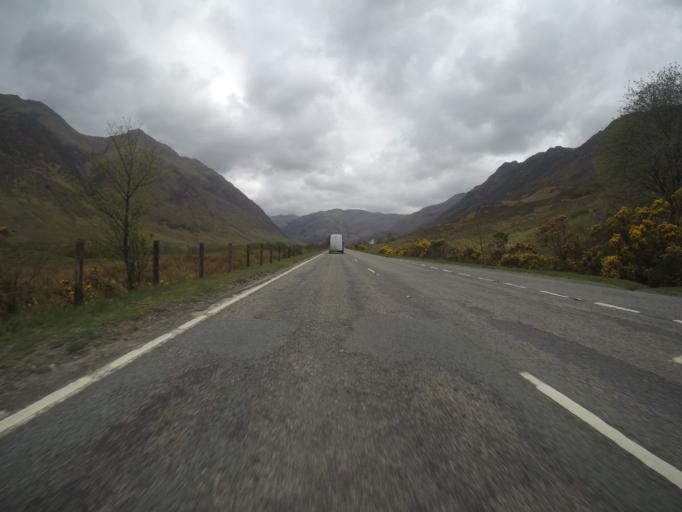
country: GB
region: Scotland
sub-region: Highland
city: Fort William
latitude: 57.1972
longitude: -5.3911
